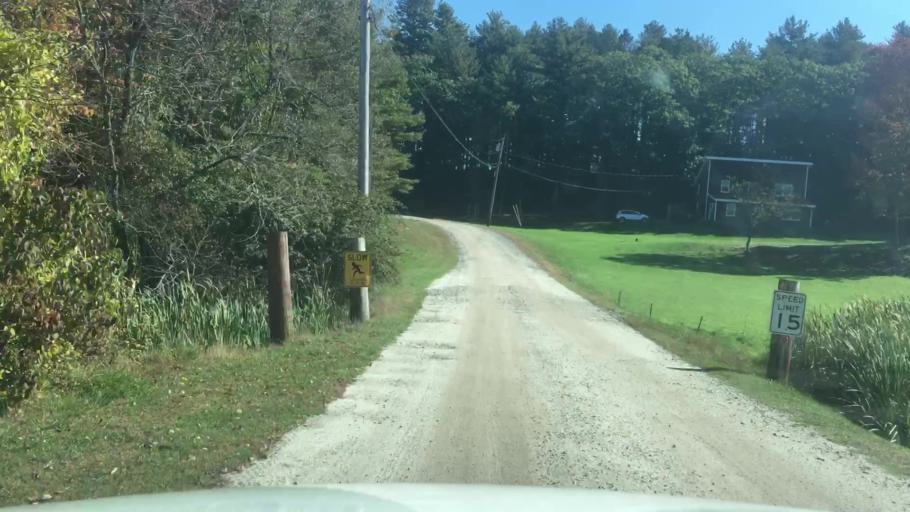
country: US
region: Maine
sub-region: Sagadahoc County
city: Bath
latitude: 43.9120
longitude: -69.8638
